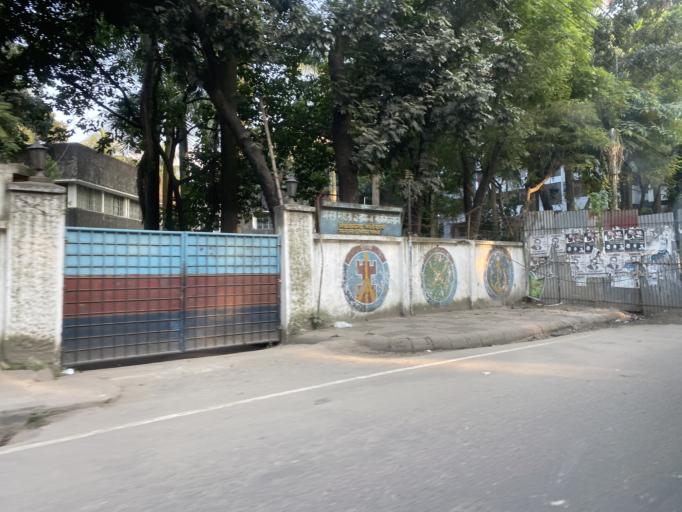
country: BD
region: Dhaka
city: Azimpur
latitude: 23.7302
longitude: 90.3955
